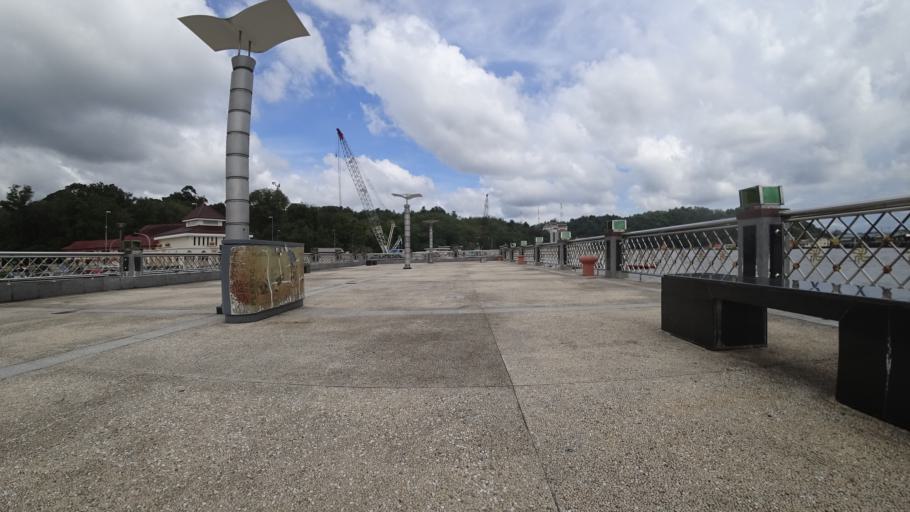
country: BN
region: Brunei and Muara
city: Bandar Seri Begawan
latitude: 4.8866
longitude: 114.9440
